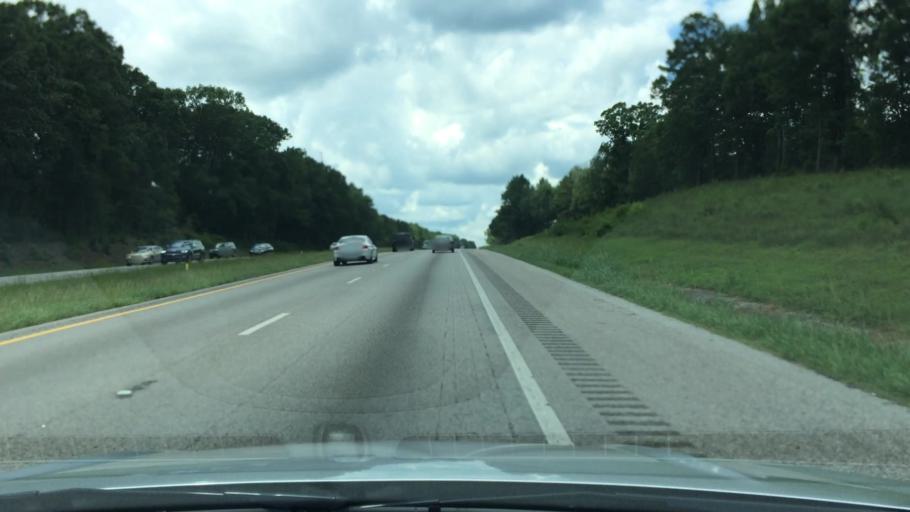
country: US
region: South Carolina
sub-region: Laurens County
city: Joanna
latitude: 34.4613
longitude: -81.7959
